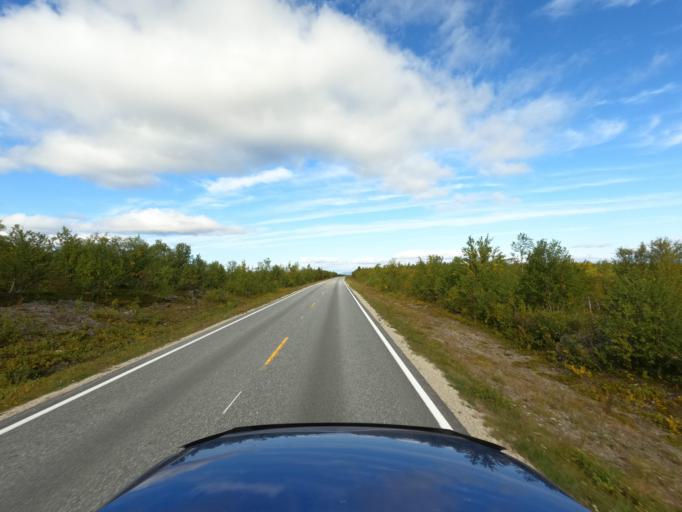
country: NO
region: Finnmark Fylke
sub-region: Karasjok
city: Karasjohka
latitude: 69.6535
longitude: 25.2785
